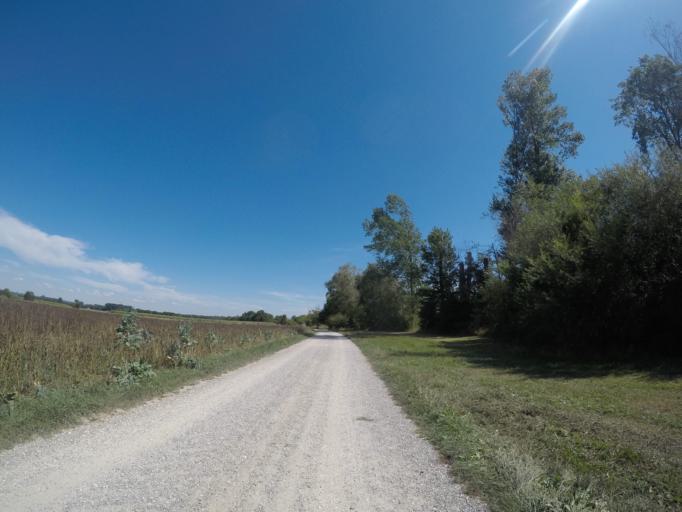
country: DE
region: Bavaria
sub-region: Swabia
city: Senden
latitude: 48.3599
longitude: 10.0552
